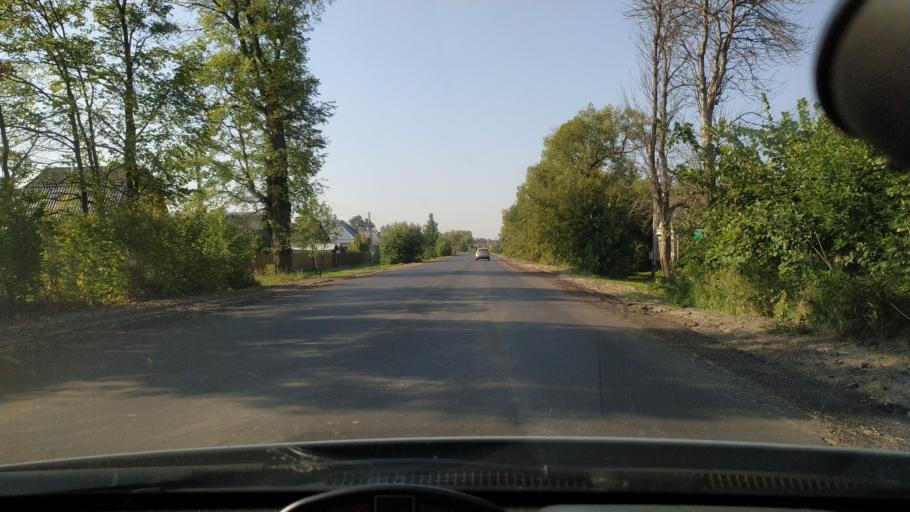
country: RU
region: Moskovskaya
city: Kerva
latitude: 55.5949
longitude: 39.7022
